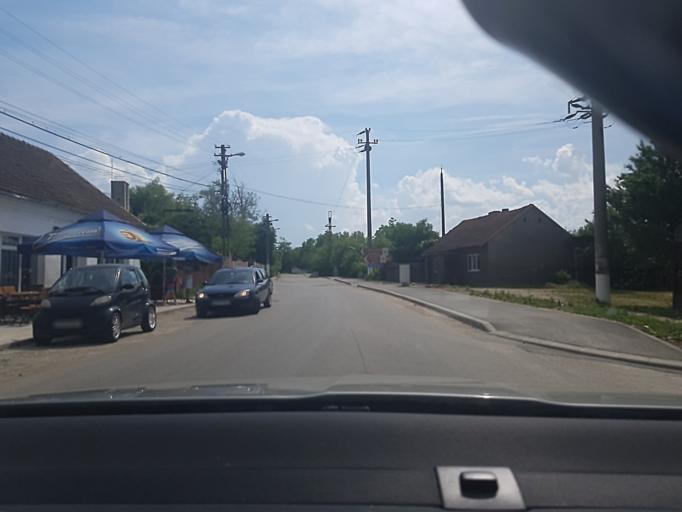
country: RO
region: Hunedoara
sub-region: Comuna Calan
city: Calan
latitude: 45.7263
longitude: 23.0170
